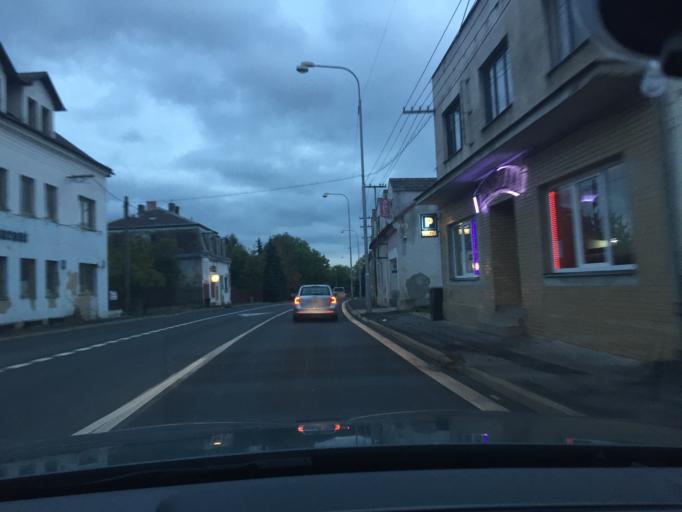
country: CZ
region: Ustecky
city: Dubi
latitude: 50.6747
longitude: 13.7911
